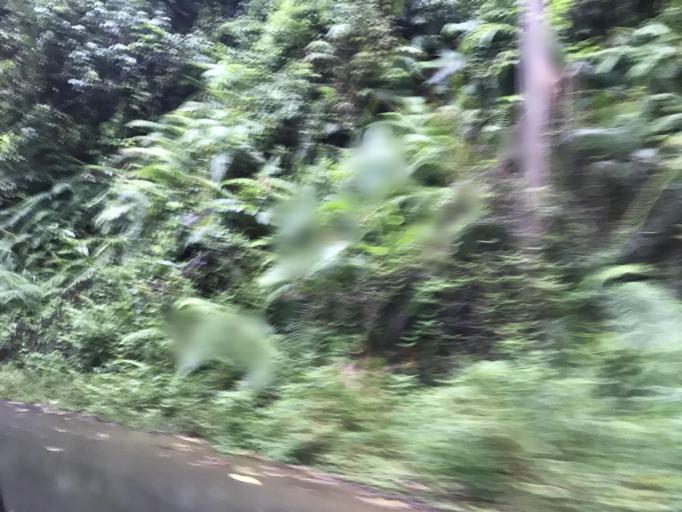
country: LK
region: Sabaragamuwa
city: Ratnapura
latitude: 6.5394
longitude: 80.2999
